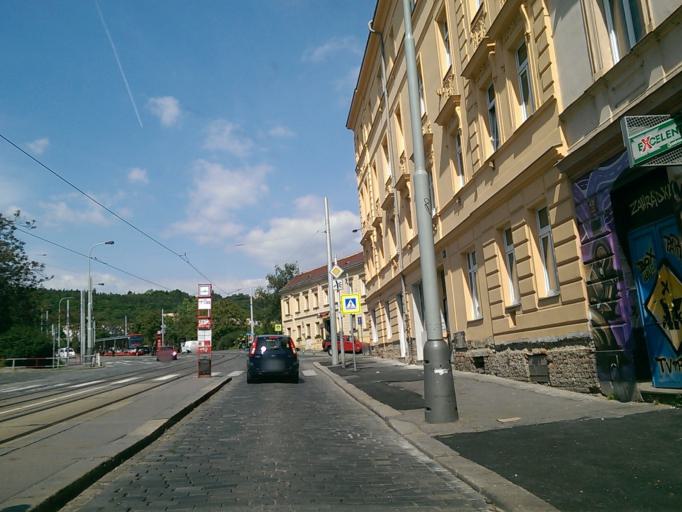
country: CZ
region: Praha
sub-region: Praha 8
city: Liben
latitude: 50.1120
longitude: 14.4753
